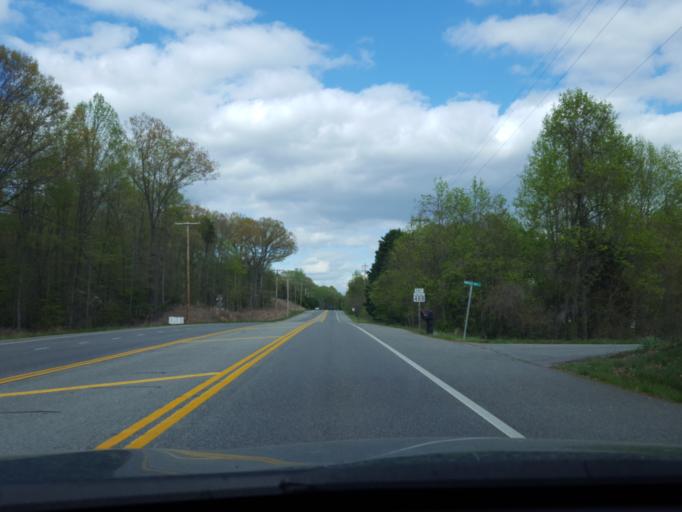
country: US
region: Maryland
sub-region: Charles County
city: Saint Charles
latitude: 38.5540
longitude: -76.8890
